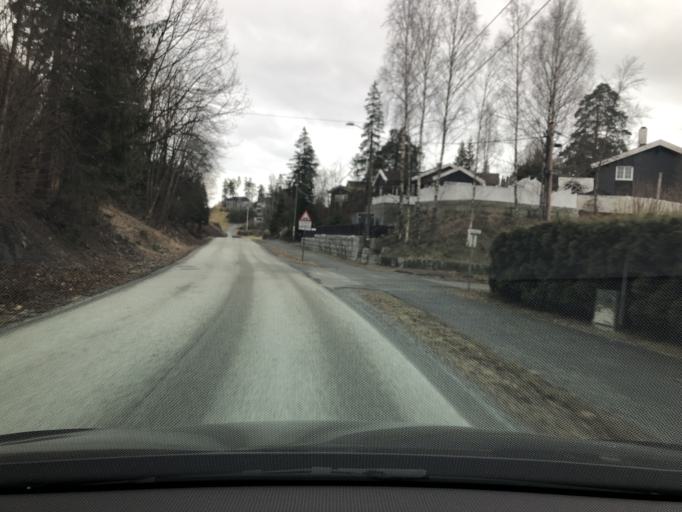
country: NO
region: Akershus
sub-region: Baerum
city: Sandvika
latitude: 59.8682
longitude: 10.5136
